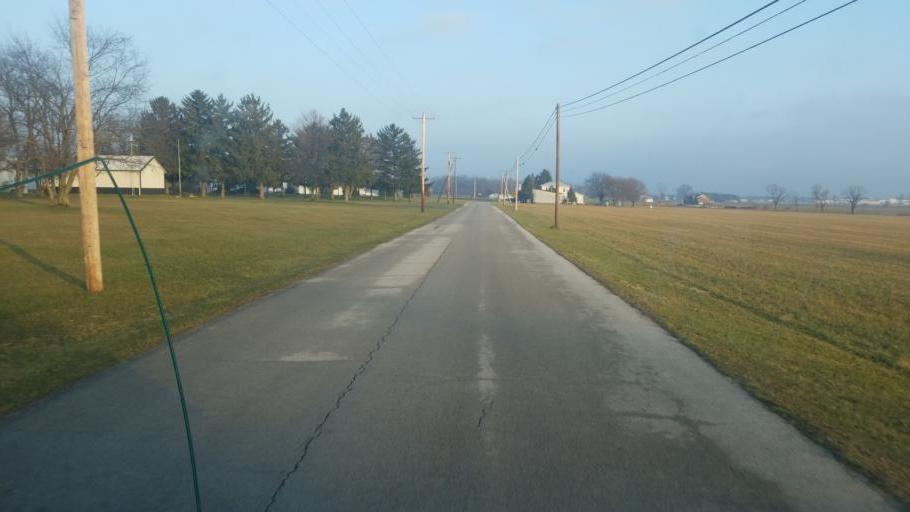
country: US
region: Ohio
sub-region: Wyandot County
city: Carey
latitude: 40.9622
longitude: -83.4239
